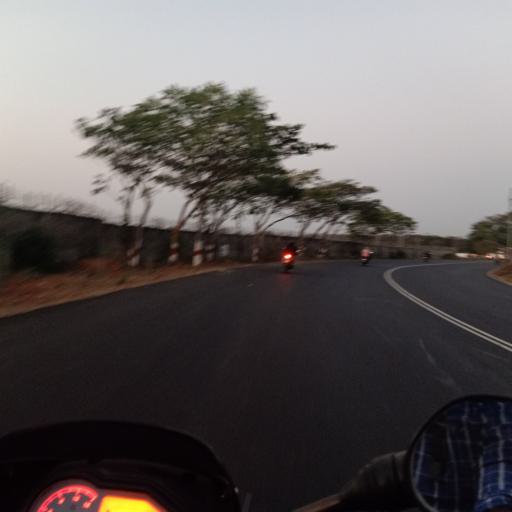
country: IN
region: Telangana
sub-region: Rangareddi
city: Secunderabad
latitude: 17.5542
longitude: 78.5365
